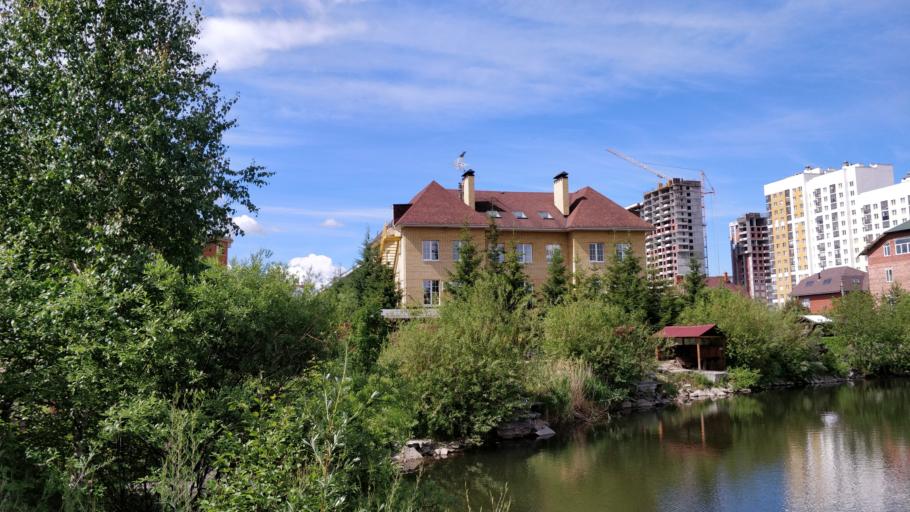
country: RU
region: Sverdlovsk
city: Sovkhoznyy
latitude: 56.7854
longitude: 60.5281
